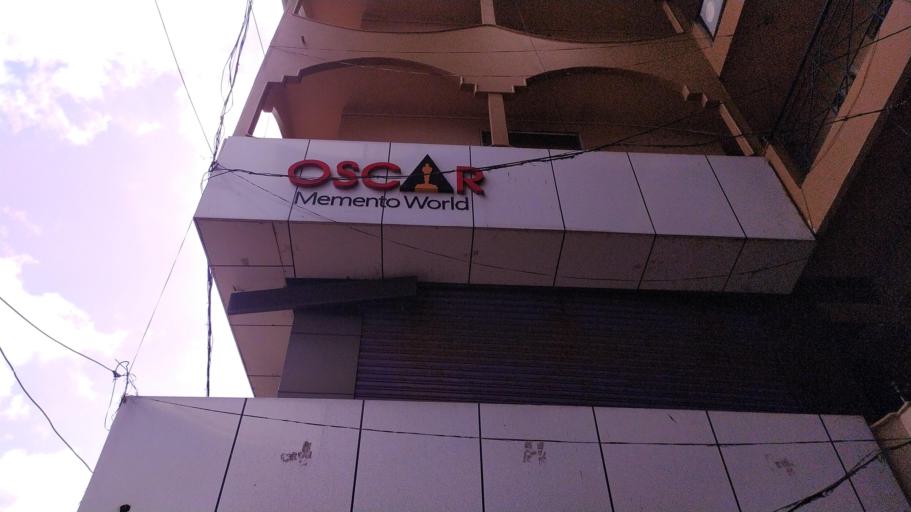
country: IN
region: Kerala
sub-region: Kasaragod District
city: Kannangad
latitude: 12.3246
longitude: 75.0860
